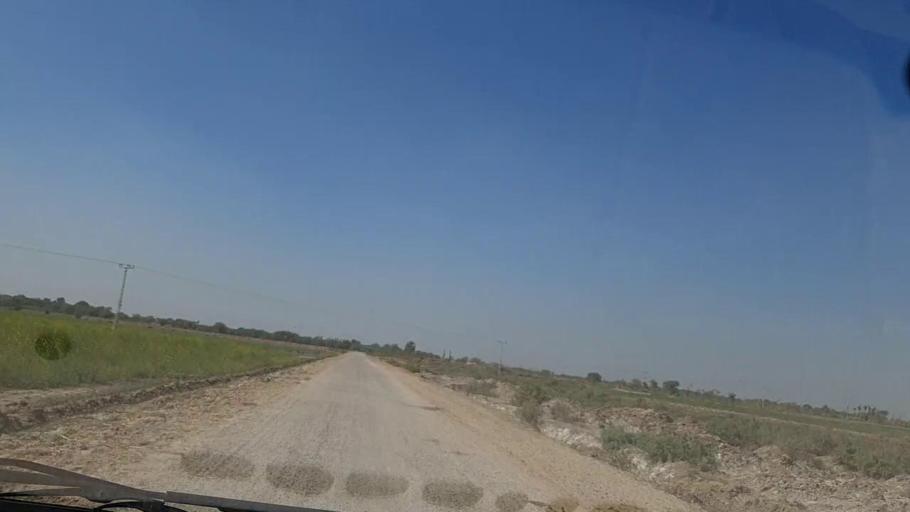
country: PK
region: Sindh
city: Mirwah Gorchani
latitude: 25.3785
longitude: 68.9781
